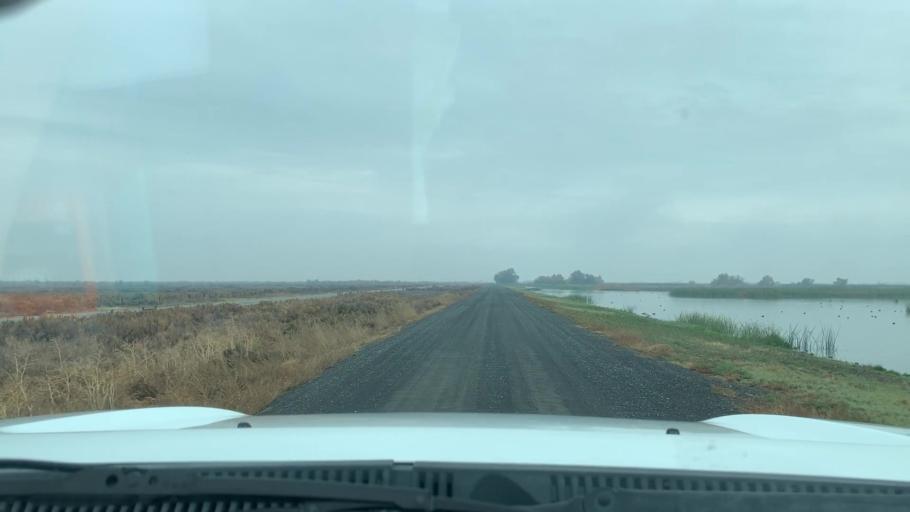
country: US
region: California
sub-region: Kern County
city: Lost Hills
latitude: 35.7396
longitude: -119.5799
